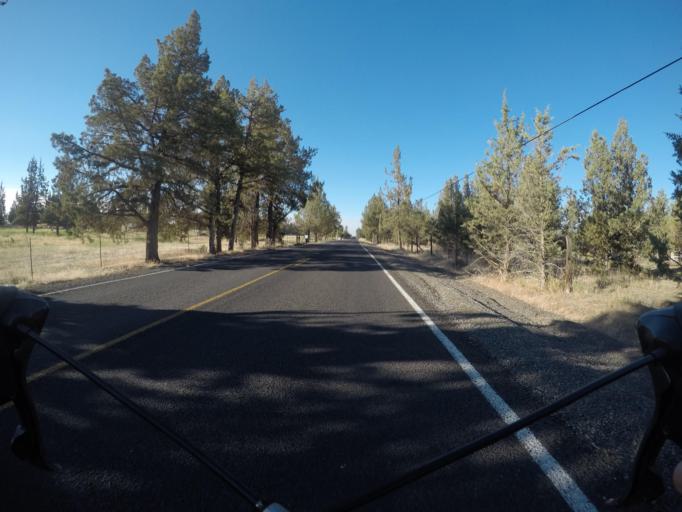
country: US
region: Oregon
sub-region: Deschutes County
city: Redmond
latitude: 44.2599
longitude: -121.2395
